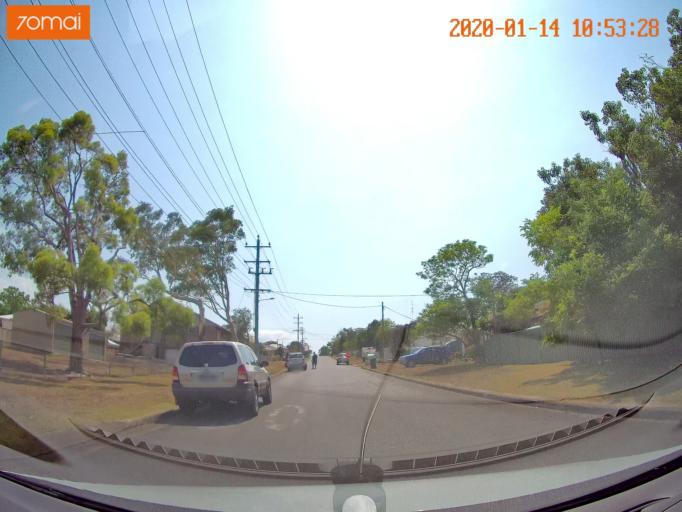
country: AU
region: New South Wales
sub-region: Lake Macquarie Shire
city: Dora Creek
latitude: -33.1017
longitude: 151.4864
